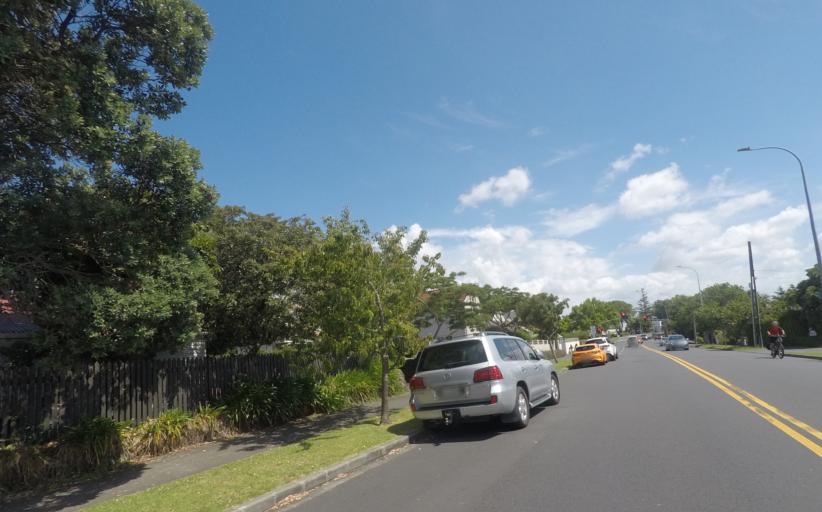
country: NZ
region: Auckland
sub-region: Auckland
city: Tamaki
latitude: -36.8740
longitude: 174.8287
